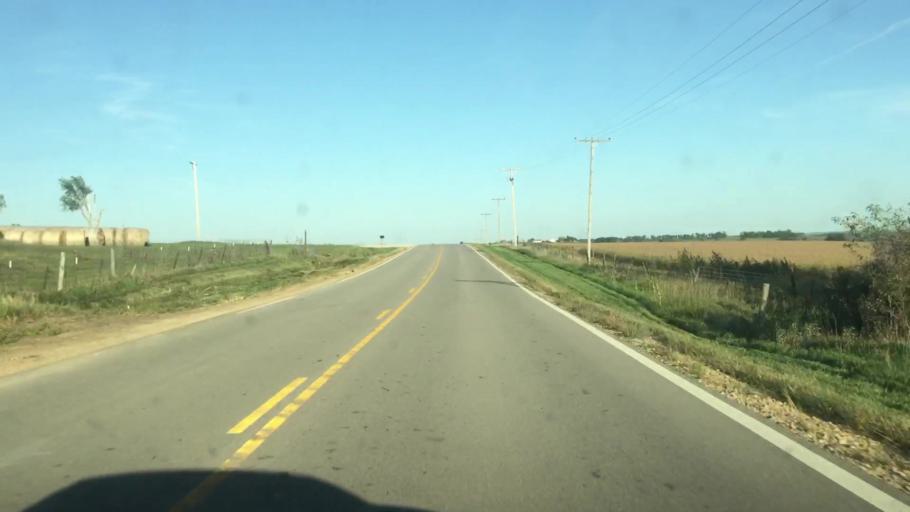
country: US
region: Kansas
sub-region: Brown County
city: Horton
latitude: 39.5876
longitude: -95.5737
